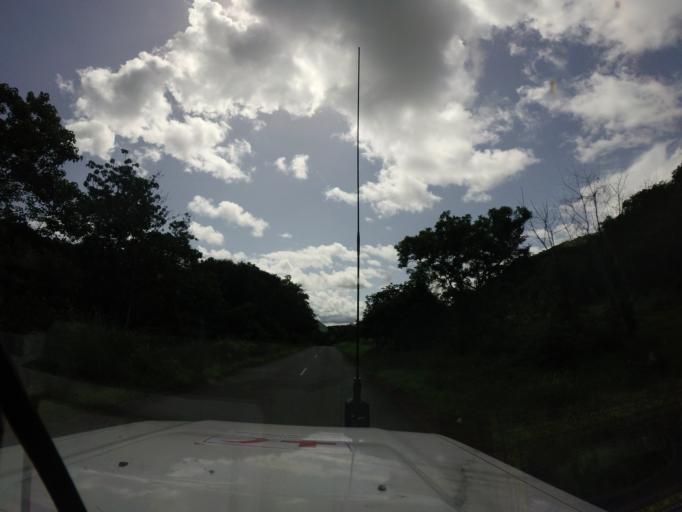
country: GN
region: Mamou
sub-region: Mamou Prefecture
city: Mamou
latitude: 10.2415
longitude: -11.8775
